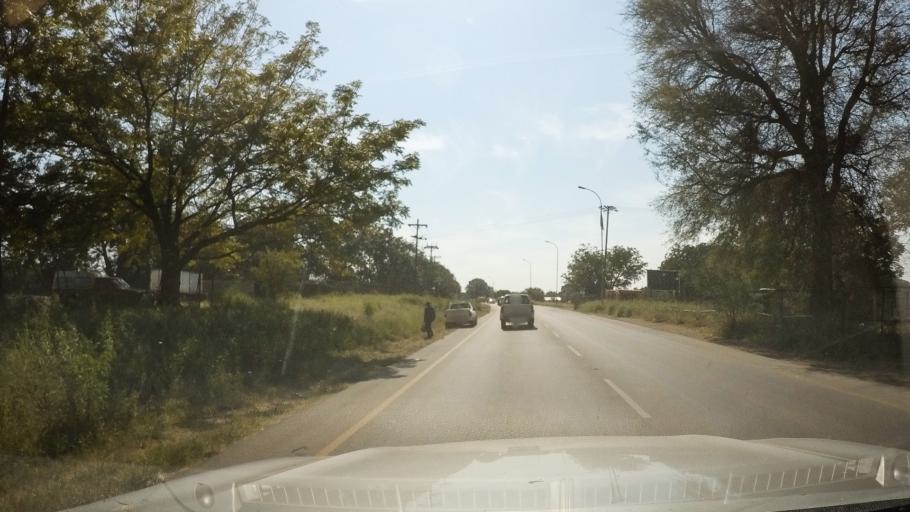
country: BW
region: South East
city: Lobatse
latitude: -25.2225
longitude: 25.6788
